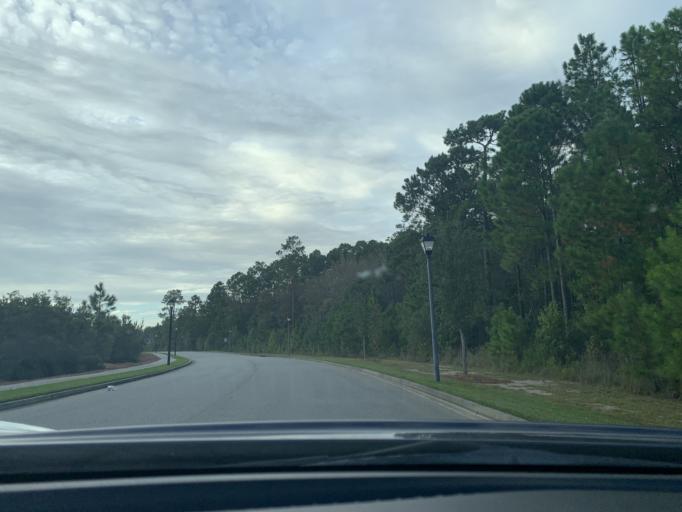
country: US
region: Georgia
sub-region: Chatham County
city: Pooler
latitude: 32.0743
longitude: -81.2595
